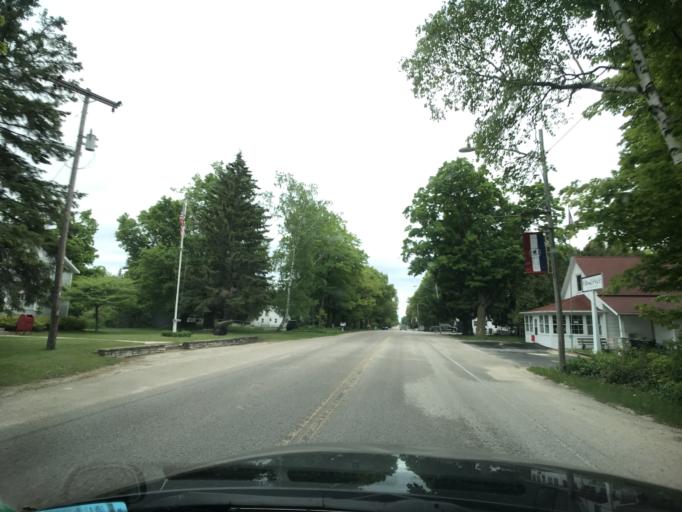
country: US
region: Michigan
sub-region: Delta County
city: Escanaba
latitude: 45.3750
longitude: -86.9307
